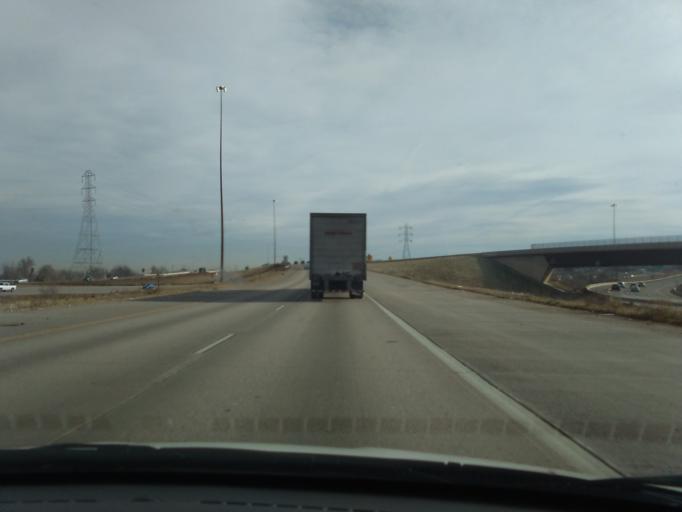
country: US
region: Colorado
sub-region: Jefferson County
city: Arvada
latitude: 39.7866
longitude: -105.0767
